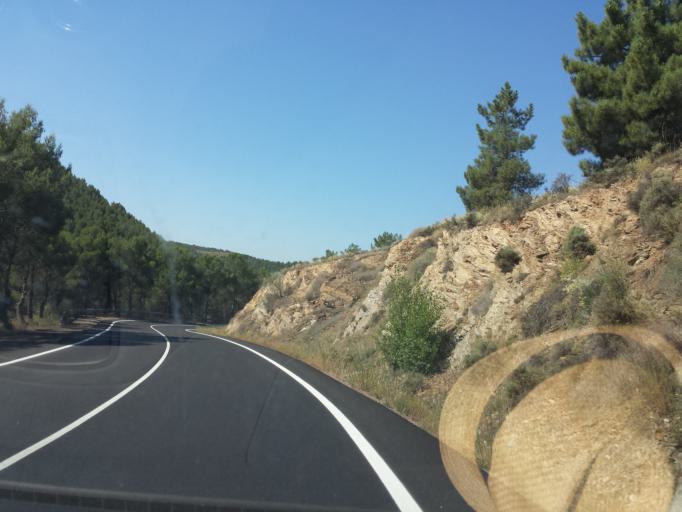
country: ES
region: Aragon
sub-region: Provincia de Zaragoza
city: Nuevalos
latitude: 41.2213
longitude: -1.7471
